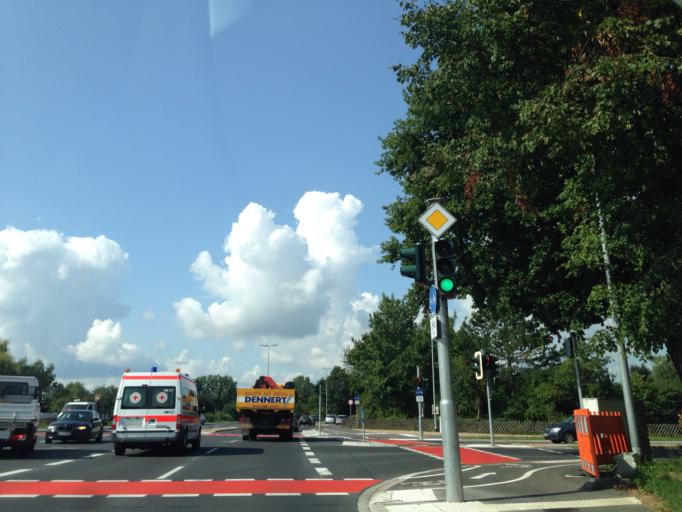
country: DE
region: Bavaria
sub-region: Upper Franconia
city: Bamberg
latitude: 49.8838
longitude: 10.9129
